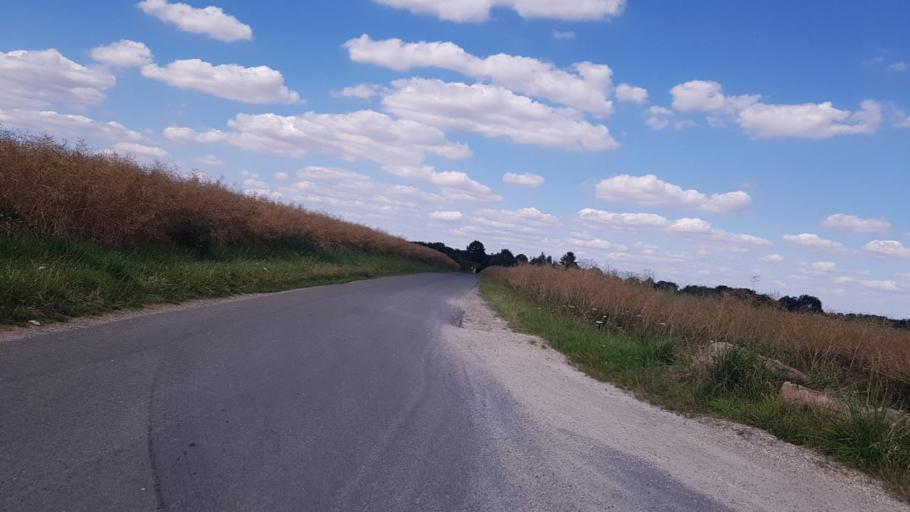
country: FR
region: Picardie
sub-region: Departement de l'Oise
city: Ver-sur-Launette
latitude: 49.1028
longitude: 2.6778
